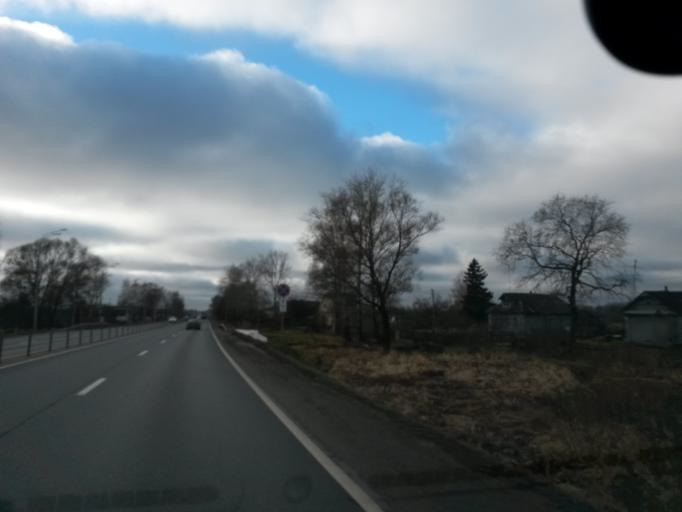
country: RU
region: Jaroslavl
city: Semibratovo
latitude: 57.3154
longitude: 39.5573
